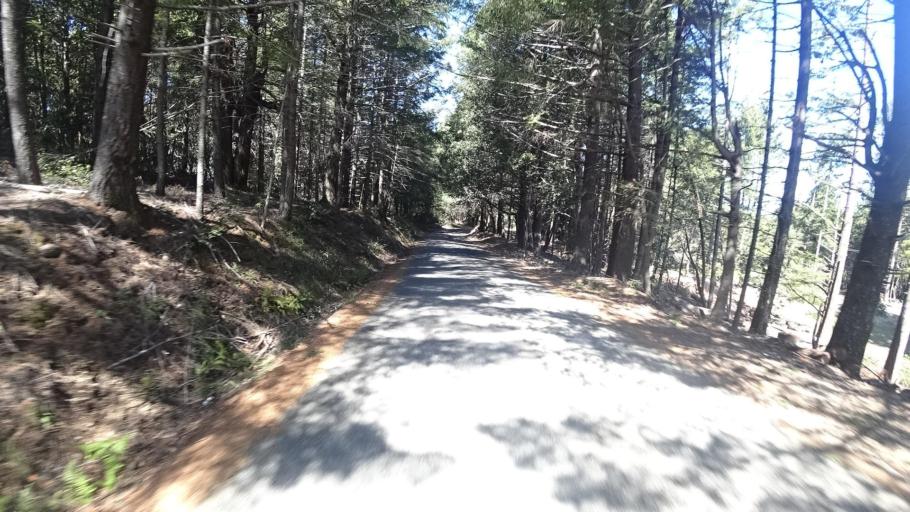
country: US
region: California
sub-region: Humboldt County
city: Redway
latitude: 40.1634
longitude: -124.0807
